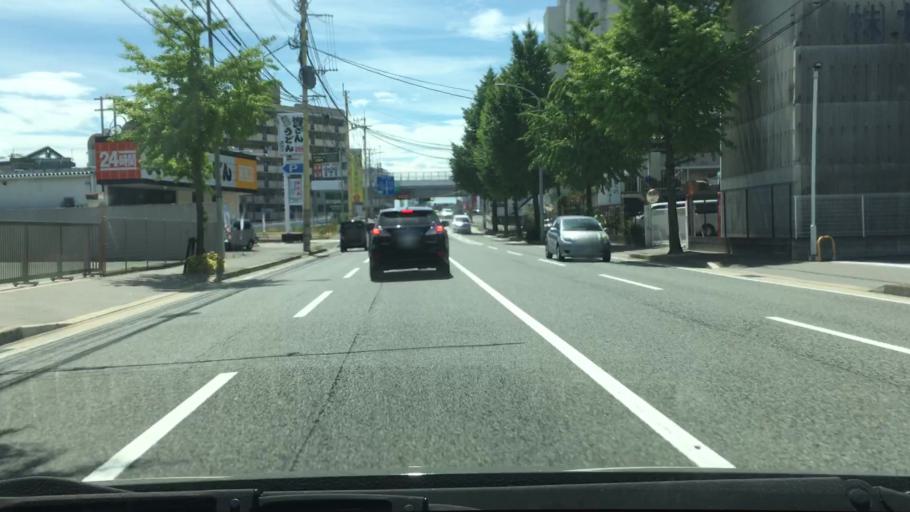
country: JP
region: Fukuoka
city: Onojo
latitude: 33.5569
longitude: 130.4520
